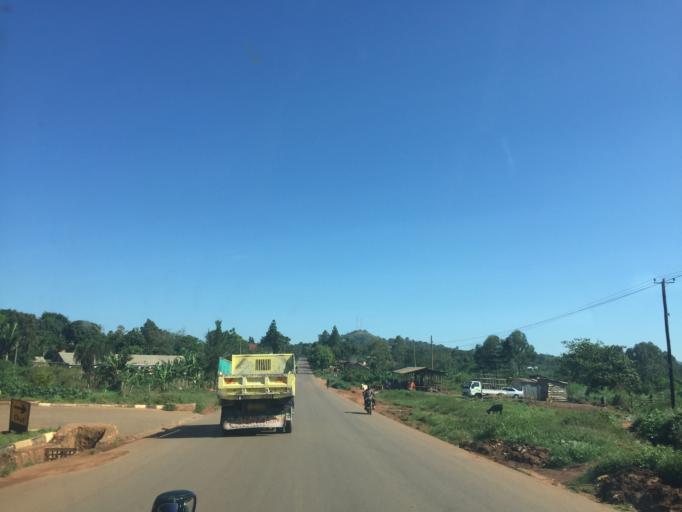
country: UG
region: Central Region
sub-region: Luwero District
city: Wobulenzi
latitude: 0.7227
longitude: 32.5282
